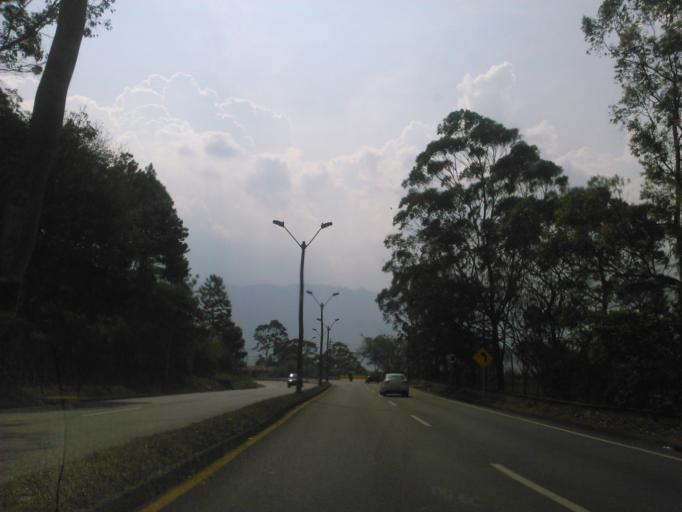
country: CO
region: Antioquia
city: Bello
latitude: 6.3237
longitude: -75.5365
